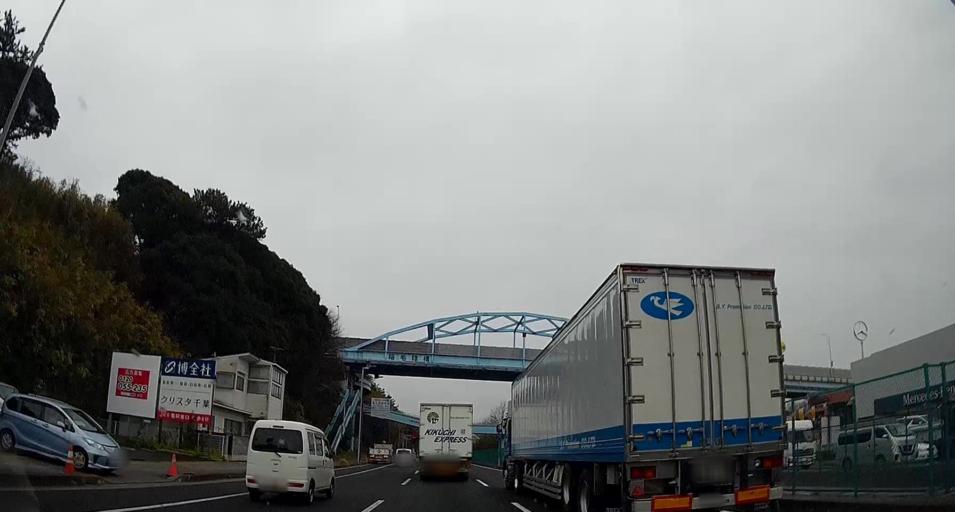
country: JP
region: Chiba
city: Chiba
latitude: 35.6327
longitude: 140.0841
